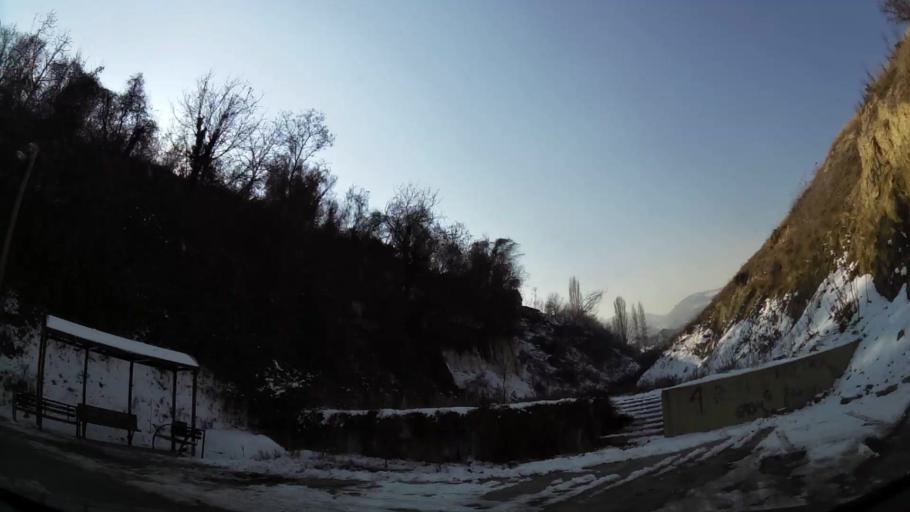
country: MK
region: Kisela Voda
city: Usje
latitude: 41.9658
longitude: 21.4450
